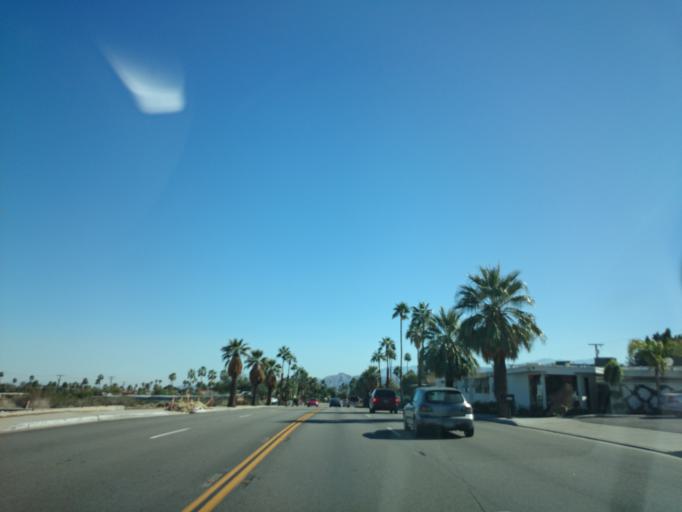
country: US
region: California
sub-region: Riverside County
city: Palm Springs
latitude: 33.8502
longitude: -116.5498
